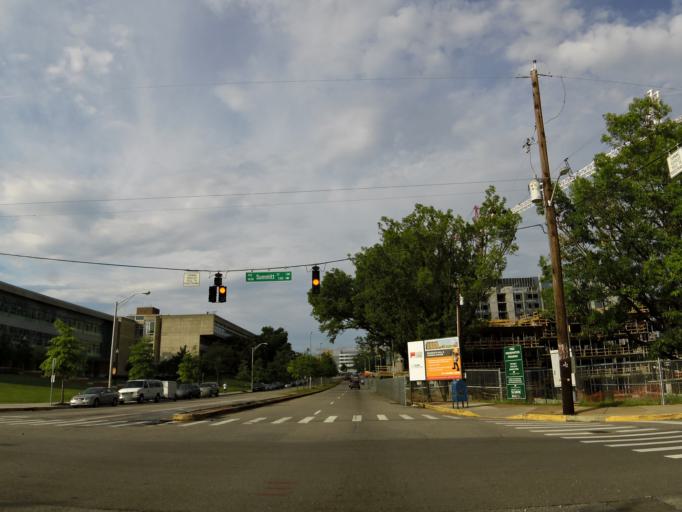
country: US
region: Tennessee
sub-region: Knox County
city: Knoxville
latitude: 35.9510
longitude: -83.9307
